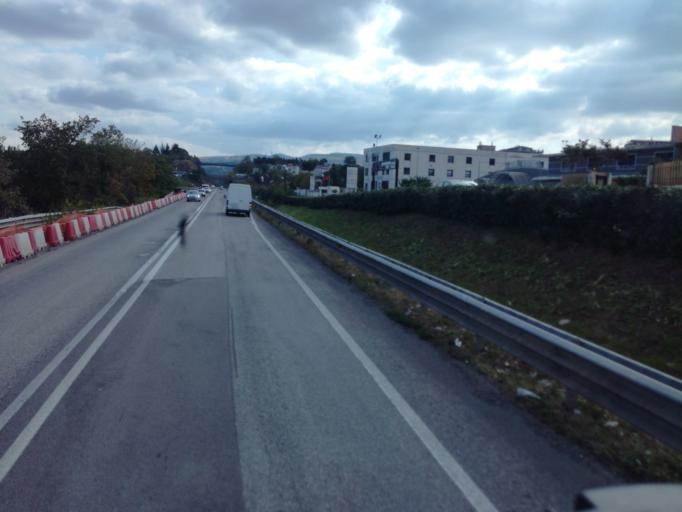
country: IT
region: Campania
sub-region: Provincia di Benevento
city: Ponte
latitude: 41.2079
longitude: 14.6935
